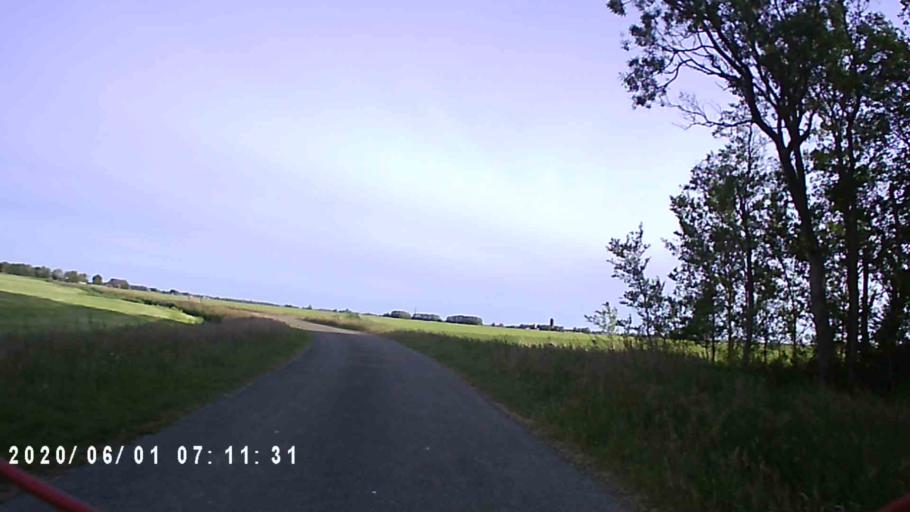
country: NL
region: Friesland
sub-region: Gemeente Dantumadiel
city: Walterswald
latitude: 53.3138
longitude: 6.0677
